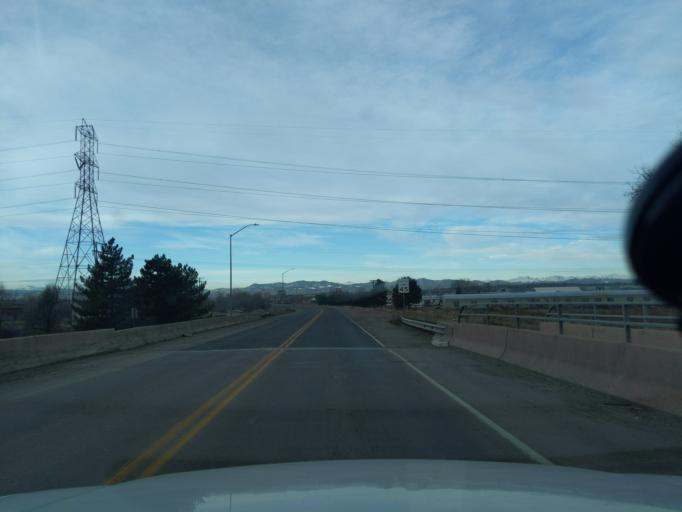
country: US
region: Colorado
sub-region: Adams County
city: Welby
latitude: 39.8308
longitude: -104.9487
